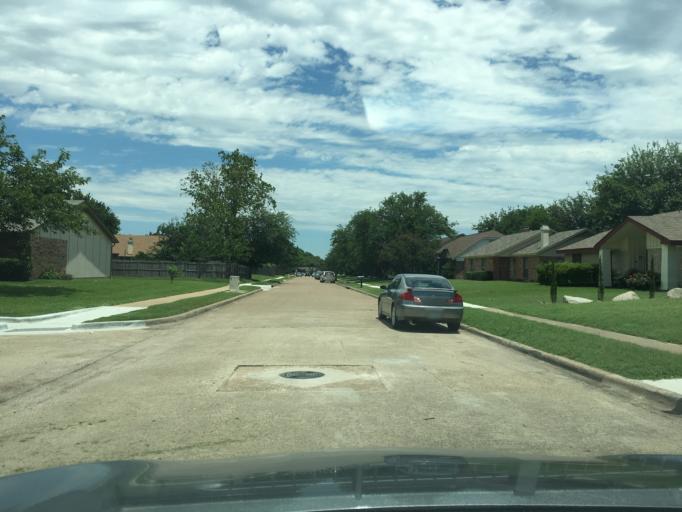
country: US
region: Texas
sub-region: Dallas County
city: Richardson
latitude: 32.9427
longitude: -96.6879
